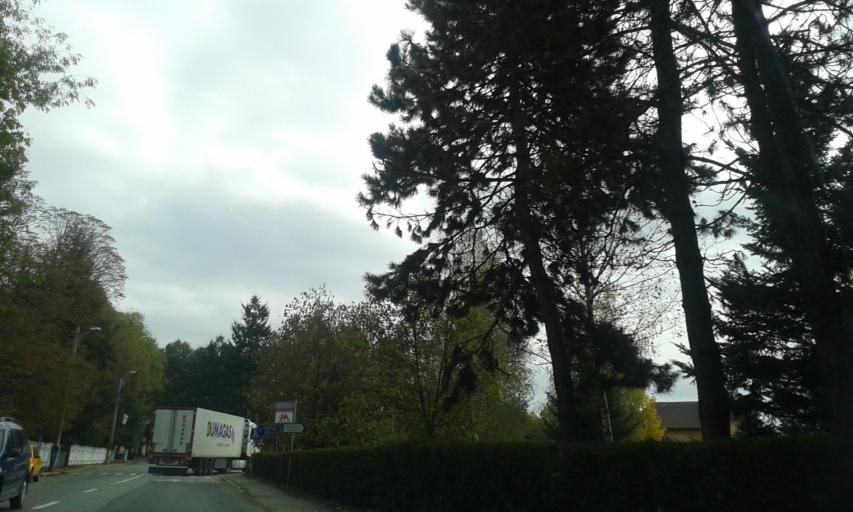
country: RO
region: Gorj
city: Targu Jiu
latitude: 45.0373
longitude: 23.2885
